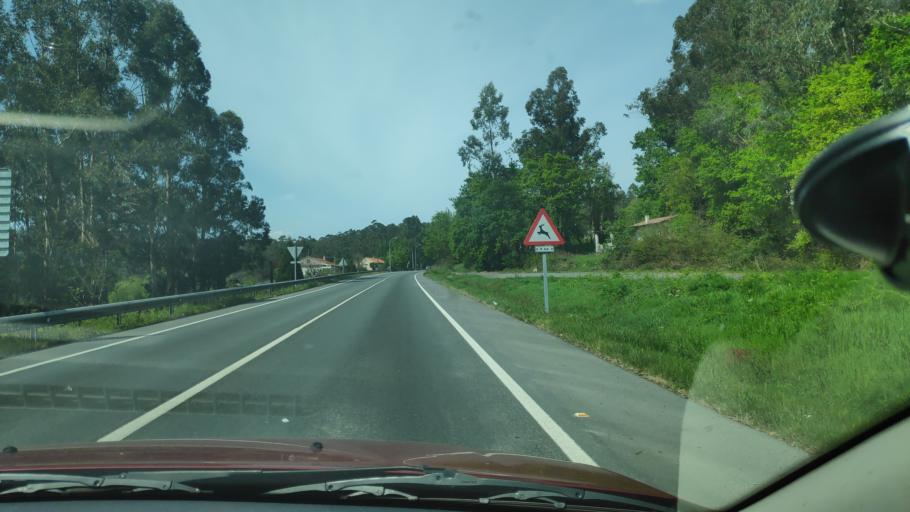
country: ES
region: Galicia
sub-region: Provincia da Coruna
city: Ames
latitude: 42.8705
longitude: -8.6585
